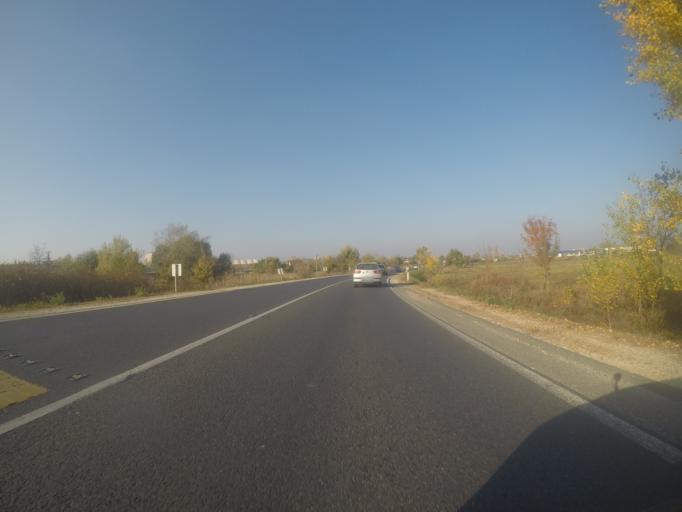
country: HU
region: Pest
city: Erd
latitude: 47.3730
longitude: 18.9332
